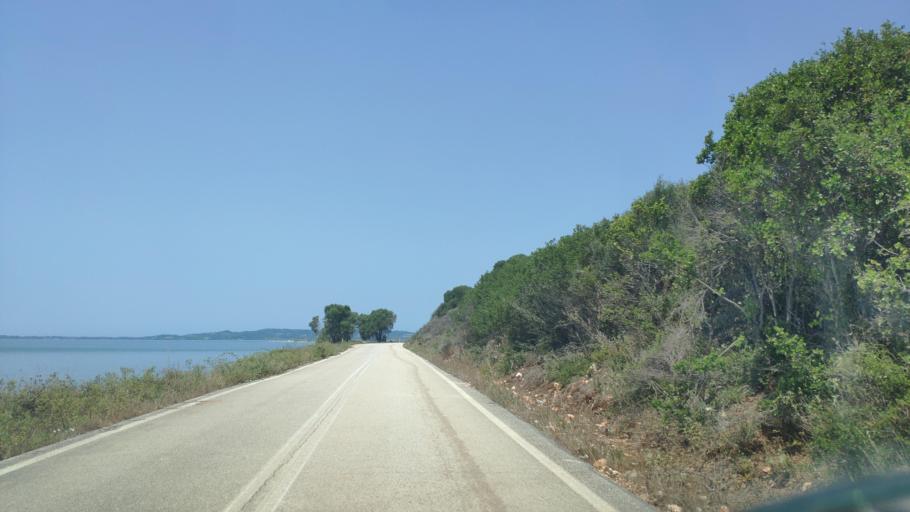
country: GR
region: Epirus
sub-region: Nomos Artas
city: Aneza
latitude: 39.0313
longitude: 20.8649
